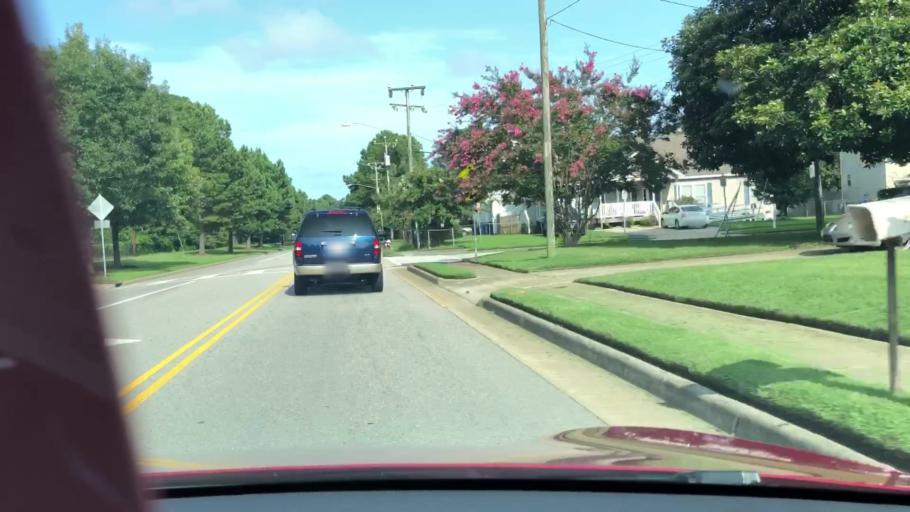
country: US
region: Virginia
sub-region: City of Virginia Beach
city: Virginia Beach
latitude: 36.8379
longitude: -75.9955
